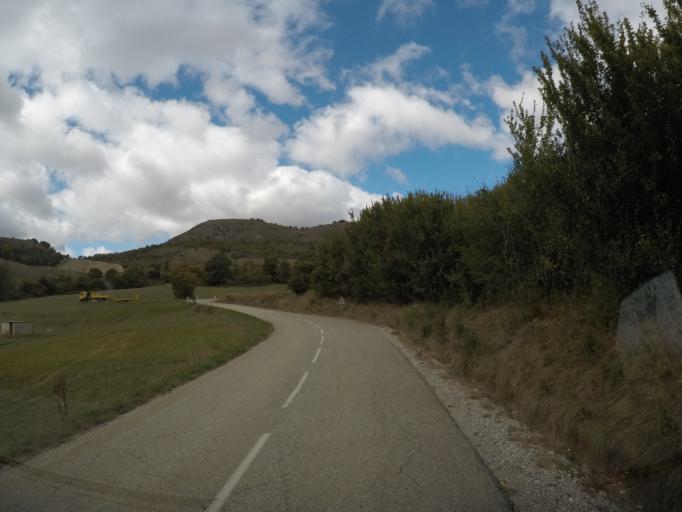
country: FR
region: Provence-Alpes-Cote d'Azur
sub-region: Departement du Vaucluse
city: Sault
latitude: 44.1844
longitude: 5.5142
